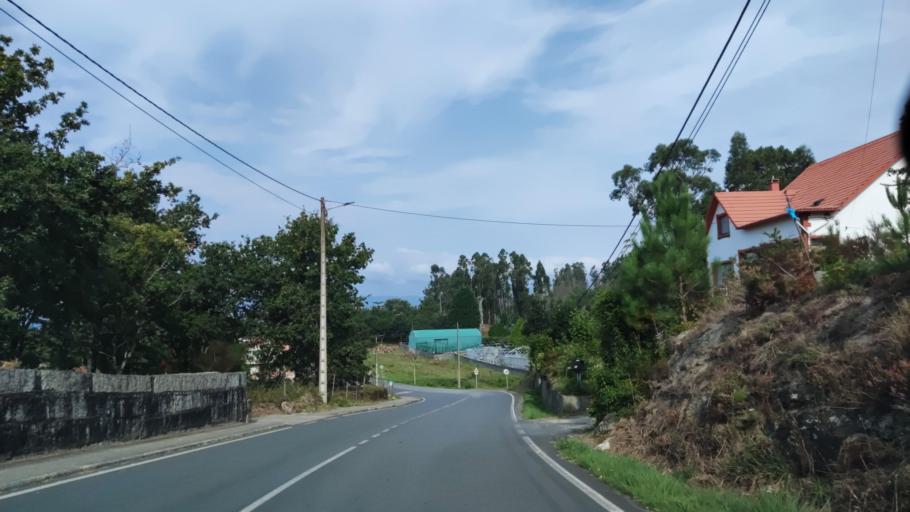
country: ES
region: Galicia
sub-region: Provincia da Coruna
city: Rianxo
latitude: 42.6468
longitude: -8.7875
